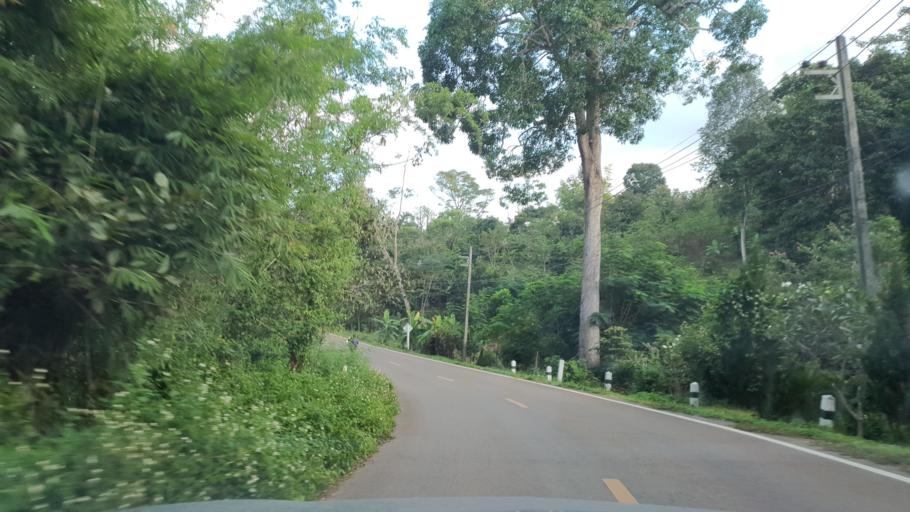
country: TH
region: Chiang Mai
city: Mae On
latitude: 18.8542
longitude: 99.2584
